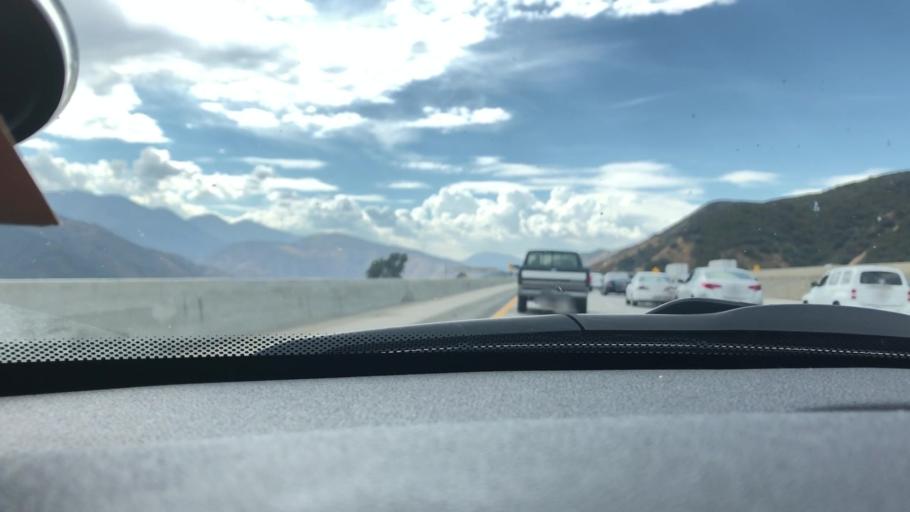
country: US
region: California
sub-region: San Bernardino County
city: Muscoy
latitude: 34.2378
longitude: -117.4270
